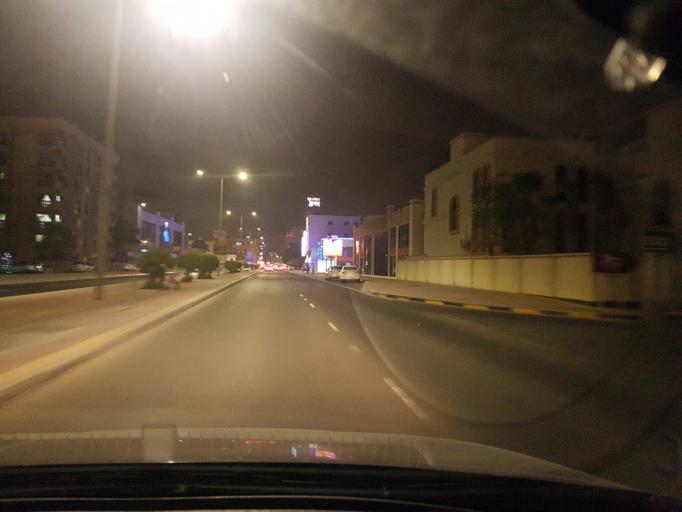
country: BH
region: Manama
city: Manama
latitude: 26.2128
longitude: 50.5912
